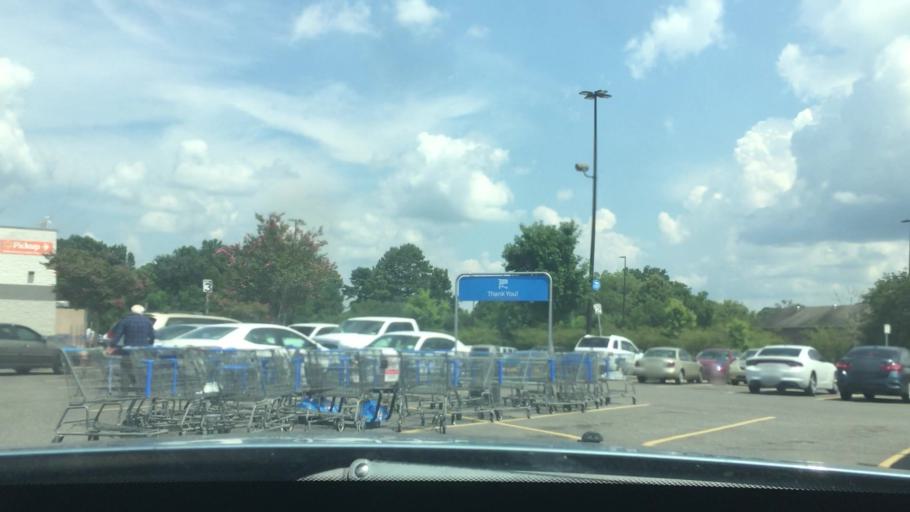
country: US
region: Louisiana
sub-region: East Baton Rouge Parish
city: Shenandoah
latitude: 30.4373
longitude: -91.0067
